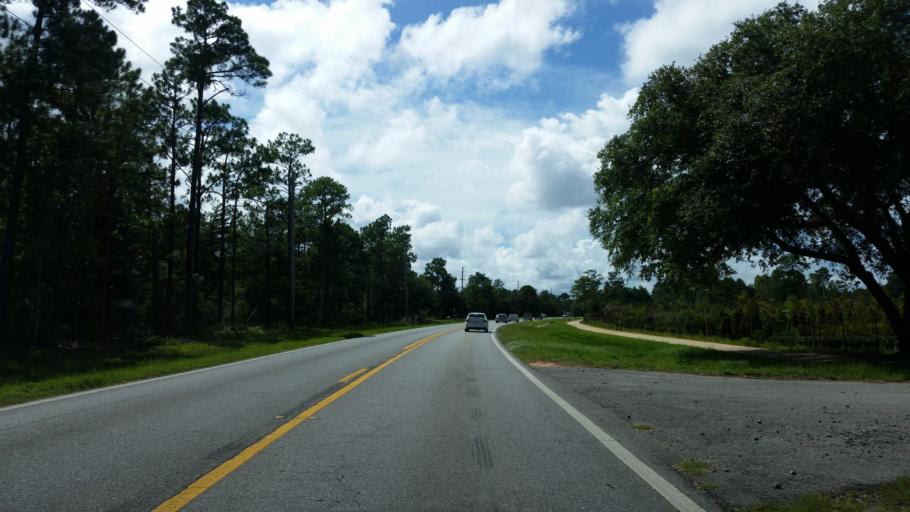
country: US
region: Florida
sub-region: Santa Rosa County
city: Holley
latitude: 30.4345
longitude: -86.9143
